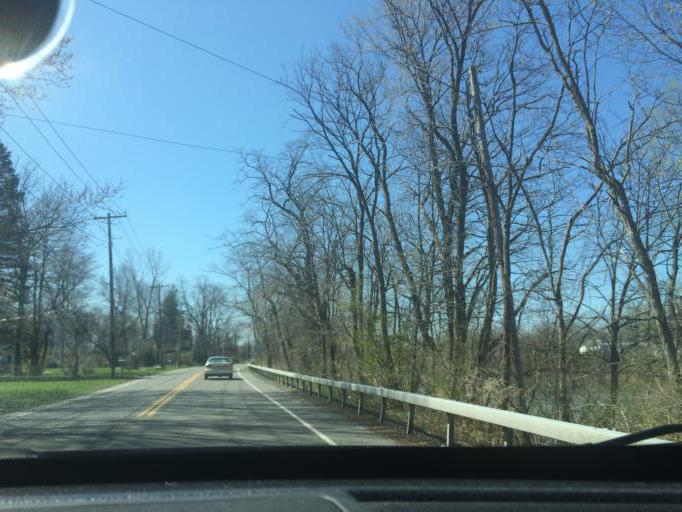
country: US
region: New York
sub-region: Monroe County
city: North Gates
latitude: 43.1008
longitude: -77.6759
